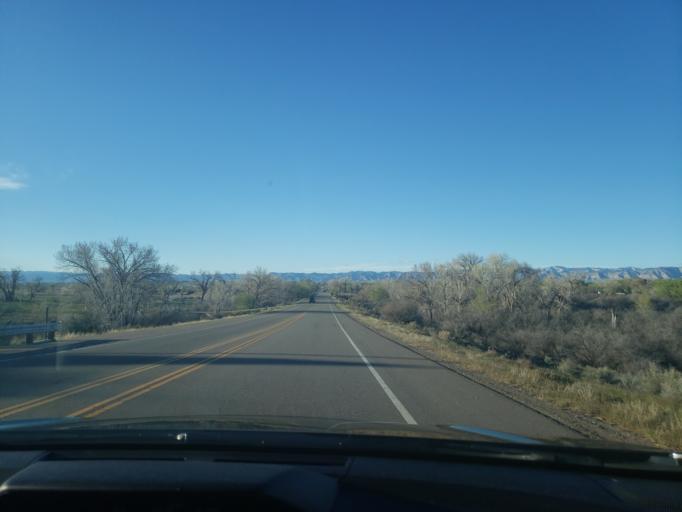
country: US
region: Colorado
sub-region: Mesa County
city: Fruita
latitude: 39.1382
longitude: -108.7383
